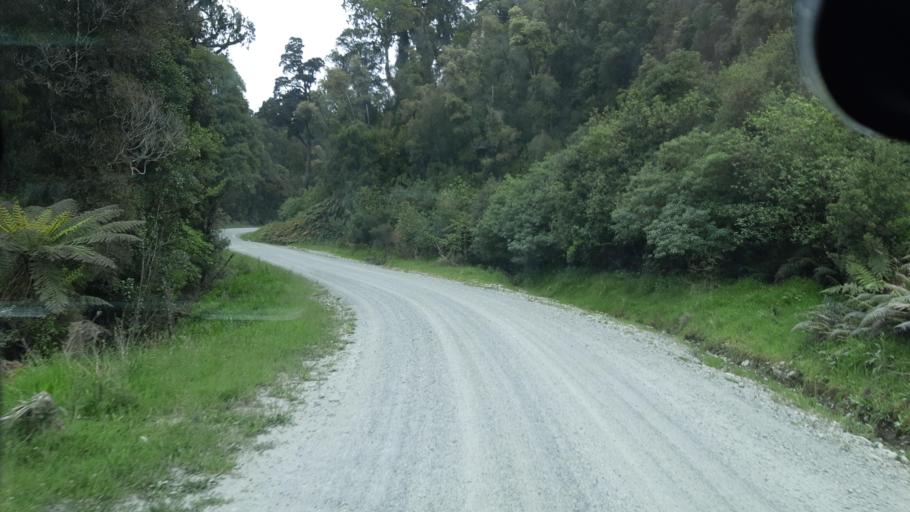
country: NZ
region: West Coast
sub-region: Grey District
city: Greymouth
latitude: -42.6494
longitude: 171.3095
